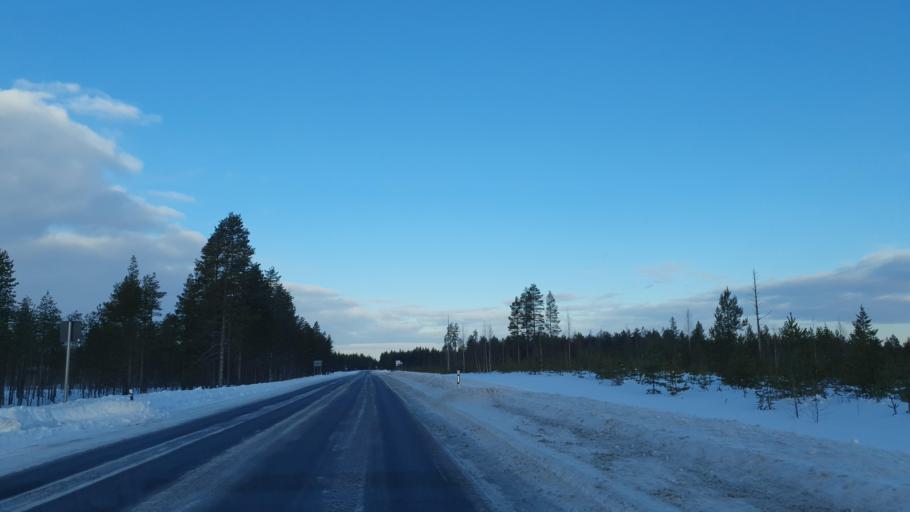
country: FI
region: Kainuu
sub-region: Kajaani
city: Vaala
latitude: 64.5790
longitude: 26.8376
